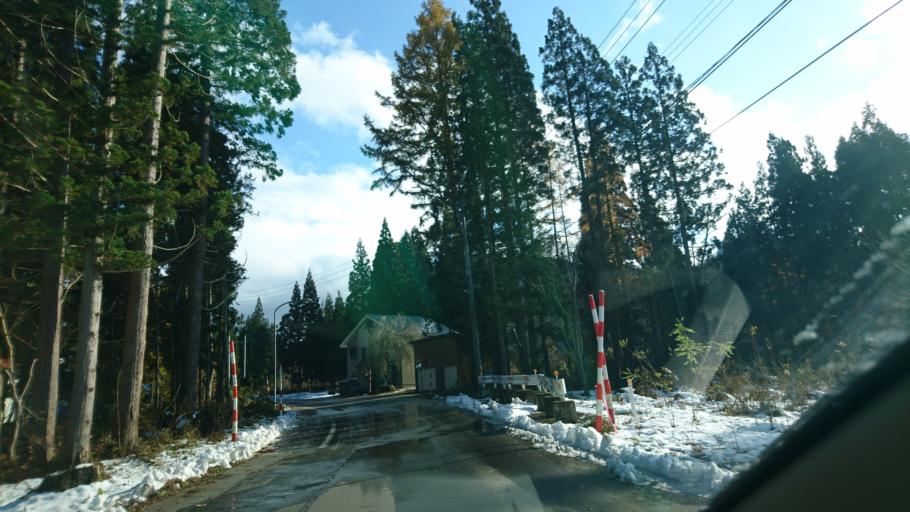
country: JP
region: Akita
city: Yokotemachi
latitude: 39.2979
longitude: 140.8317
